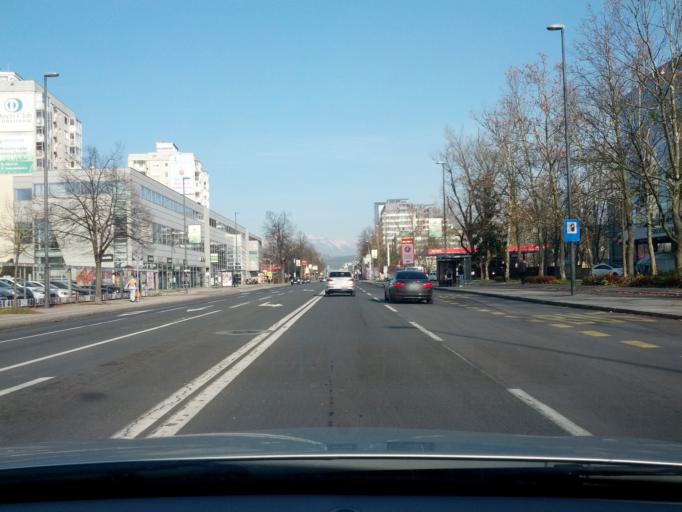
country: SI
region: Ljubljana
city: Ljubljana
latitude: 46.0769
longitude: 14.5118
